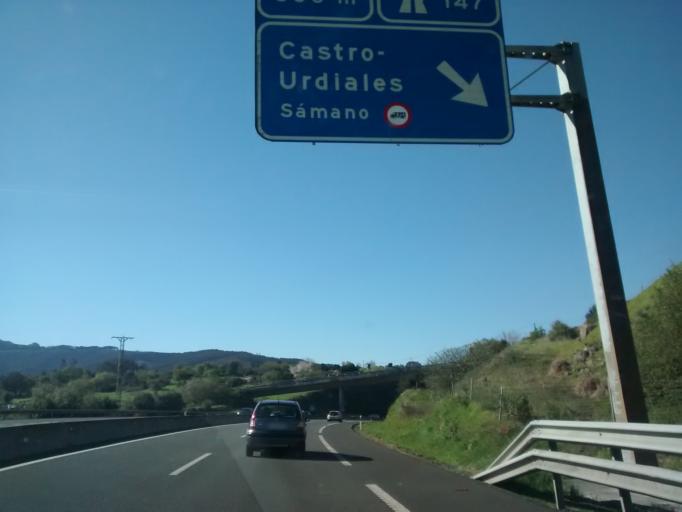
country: ES
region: Cantabria
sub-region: Provincia de Cantabria
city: Castro-Urdiales
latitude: 43.3568
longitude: -3.2176
